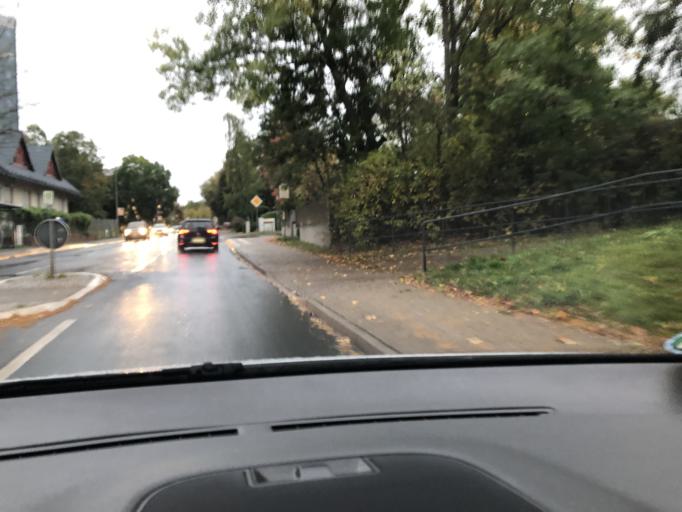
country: DE
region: Thuringia
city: Ilmenau
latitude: 50.6800
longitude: 10.9193
